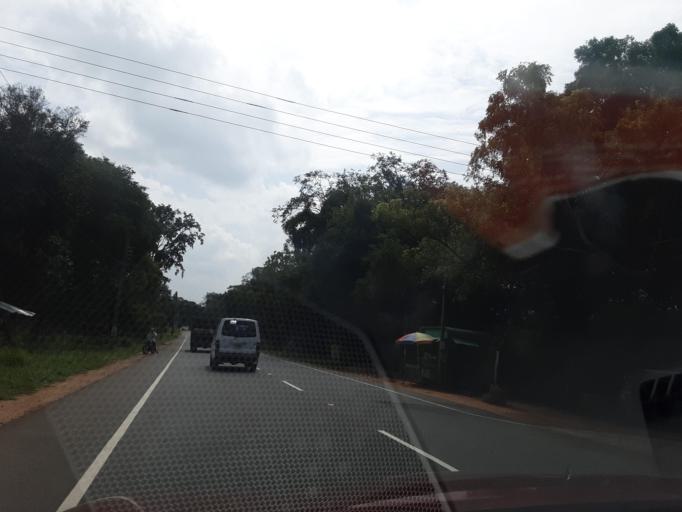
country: LK
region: North Central
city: Anuradhapura
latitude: 8.4877
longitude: 80.5108
